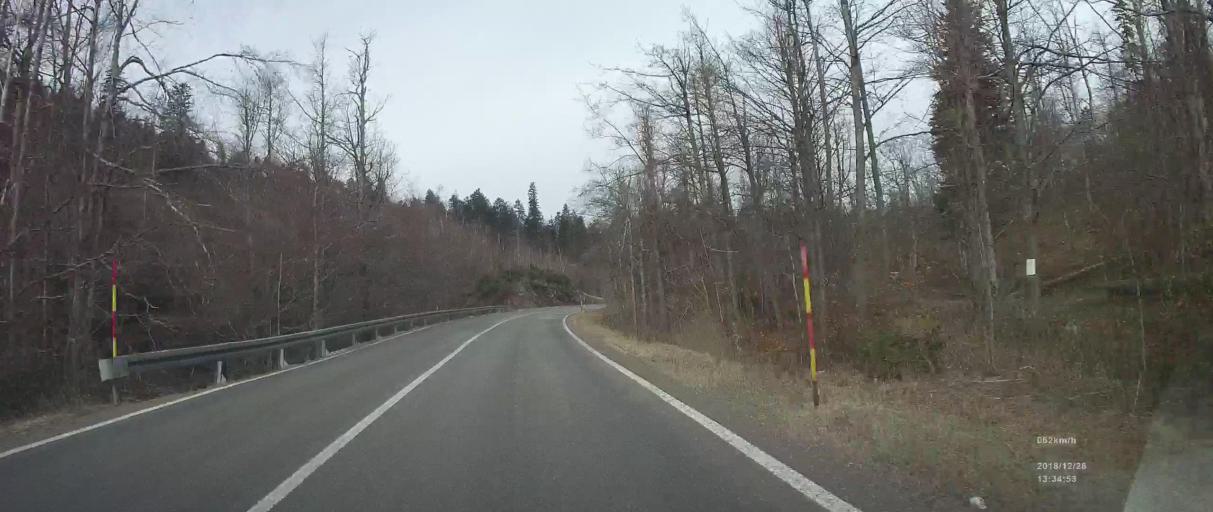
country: HR
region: Primorsko-Goranska
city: Hreljin
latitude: 45.3445
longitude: 14.6899
